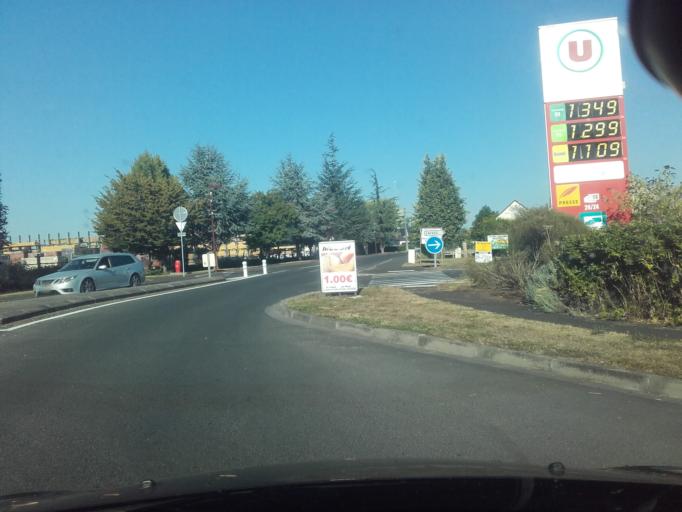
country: FR
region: Centre
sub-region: Departement d'Indre-et-Loire
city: Ambillou
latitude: 47.4501
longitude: 0.4557
